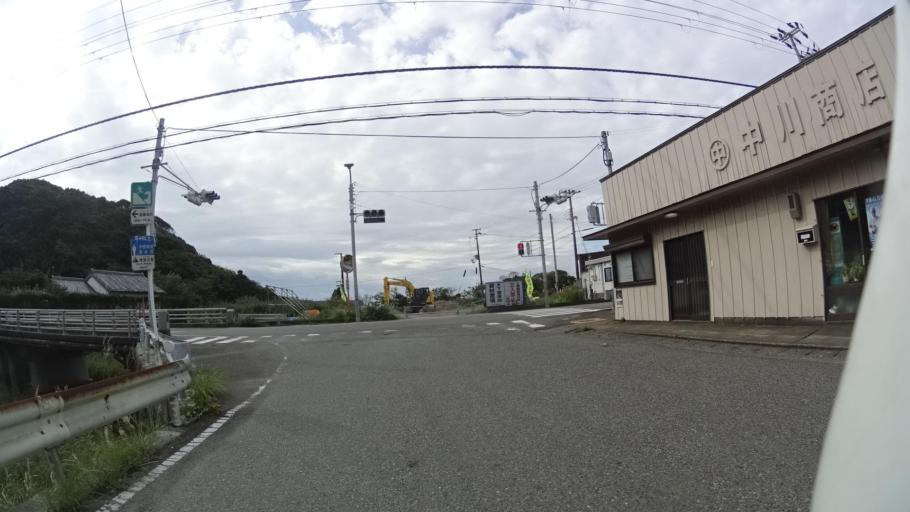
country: JP
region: Wakayama
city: Shingu
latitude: 33.4836
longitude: 135.7629
